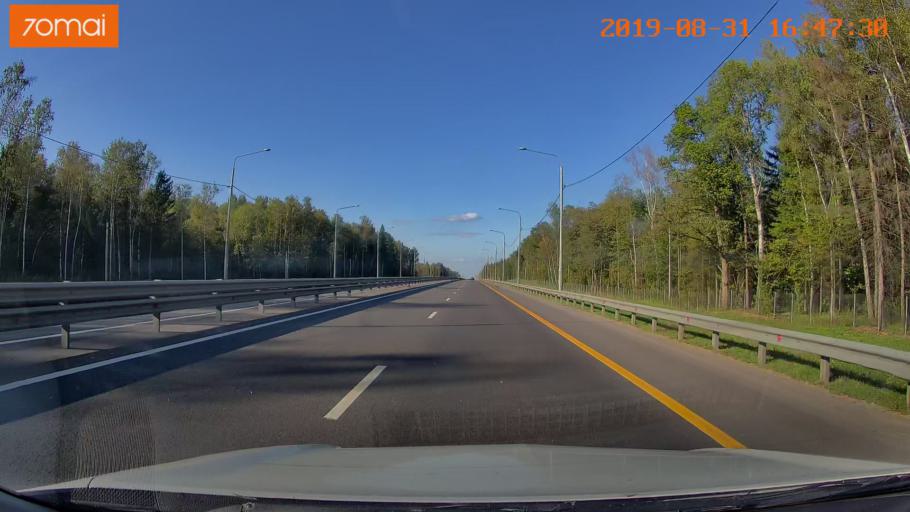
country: RU
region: Kaluga
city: Pyatovskiy
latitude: 54.6553
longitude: 36.1394
